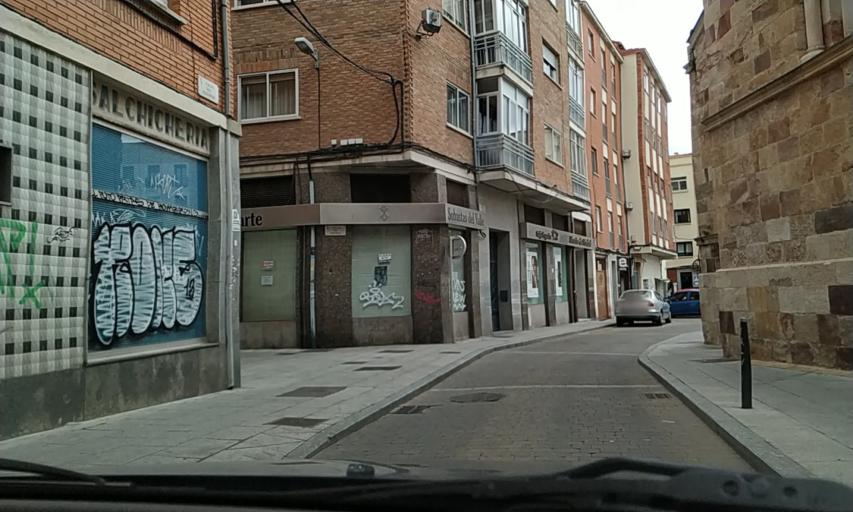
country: ES
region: Castille and Leon
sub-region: Provincia de Zamora
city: Zamora
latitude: 41.5062
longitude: -5.7453
